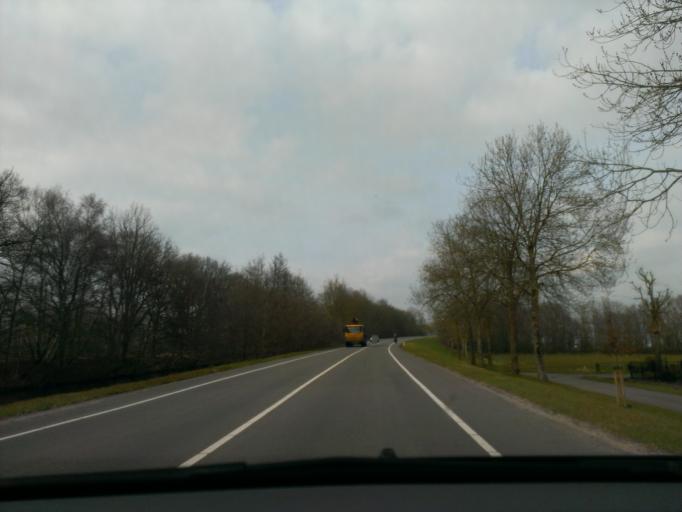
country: NL
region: Gelderland
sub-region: Gemeente Epe
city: Emst
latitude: 52.3069
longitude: 6.0047
